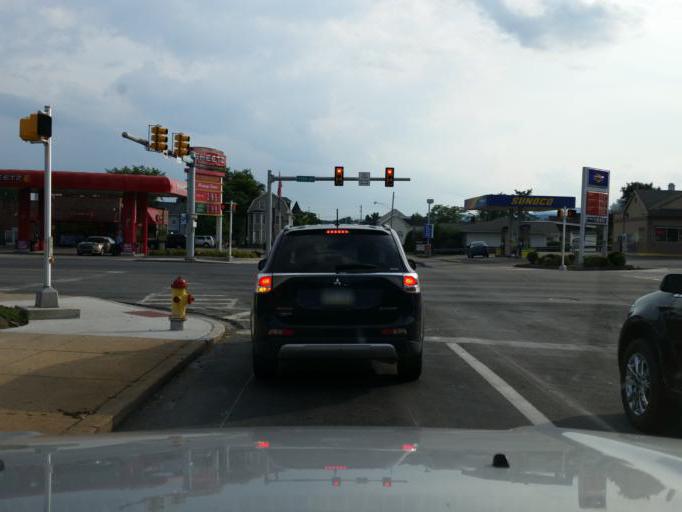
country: US
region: Pennsylvania
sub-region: Blair County
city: Altoona
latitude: 40.5088
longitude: -78.4008
